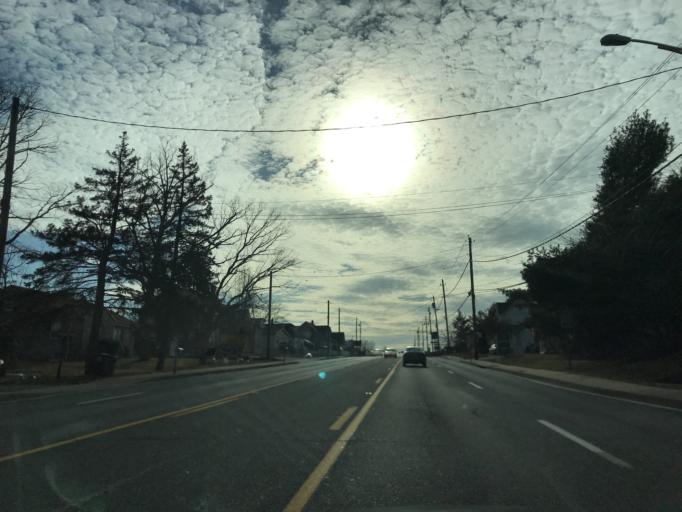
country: US
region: Maryland
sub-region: Baltimore County
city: Perry Hall
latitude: 39.4022
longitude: -76.4760
